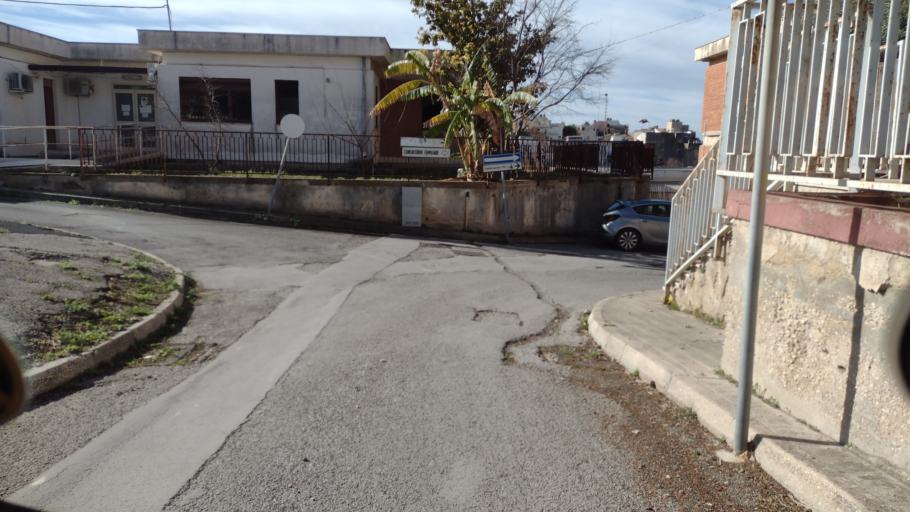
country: IT
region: Sicily
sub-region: Provincia di Siracusa
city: Noto
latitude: 36.8967
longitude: 15.0683
